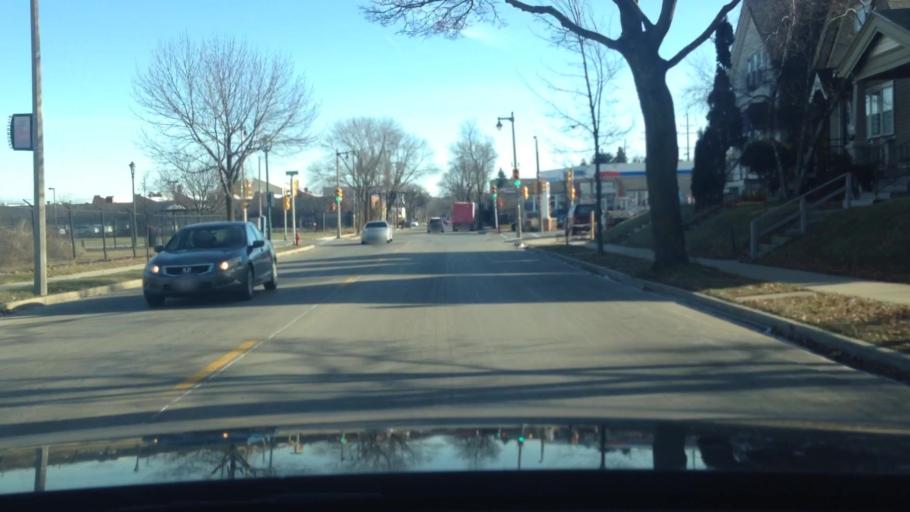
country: US
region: Wisconsin
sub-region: Milwaukee County
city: Shorewood
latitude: 43.0820
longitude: -87.9059
